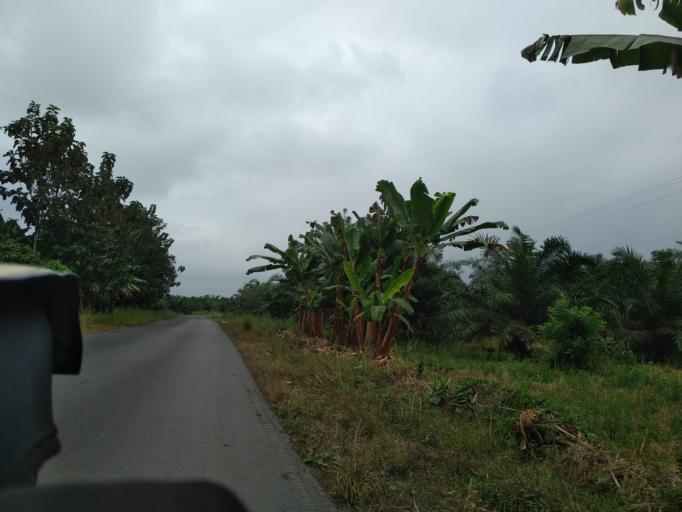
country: EC
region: Los Rios
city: Quevedo
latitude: -0.9668
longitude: -79.3514
